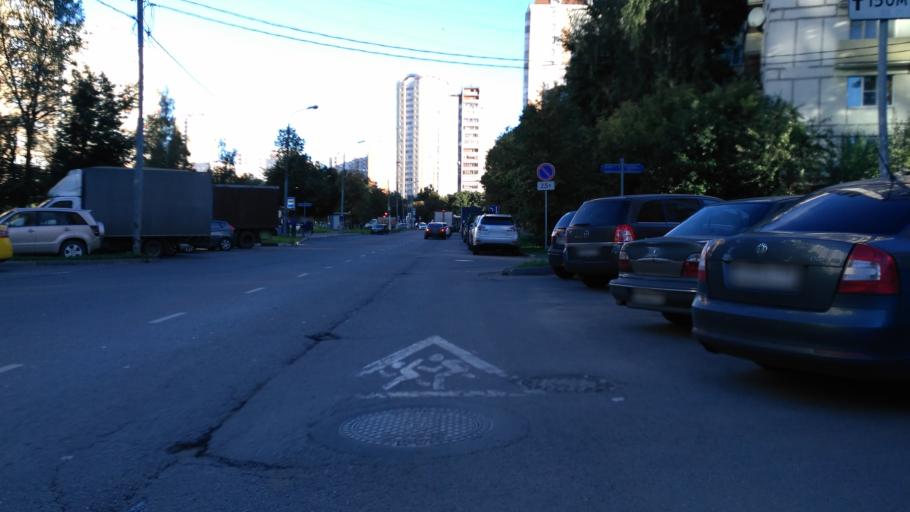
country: RU
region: Moskovskaya
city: Vostochnoe Degunino
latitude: 55.8705
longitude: 37.5556
